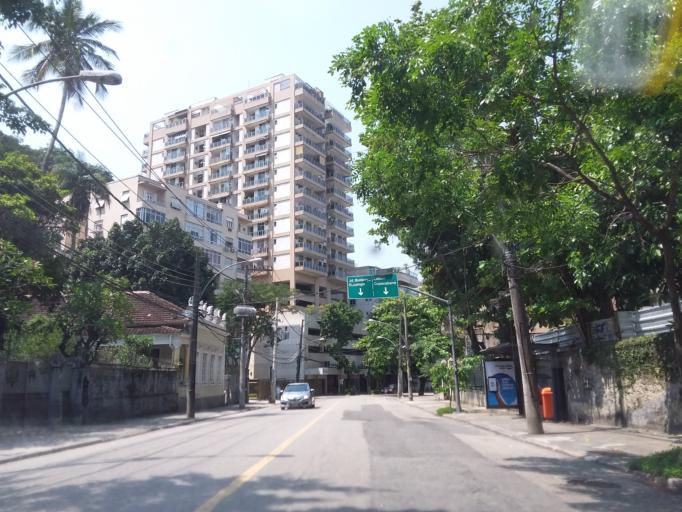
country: BR
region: Rio de Janeiro
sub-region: Rio De Janeiro
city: Rio de Janeiro
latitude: -22.9779
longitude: -43.2331
